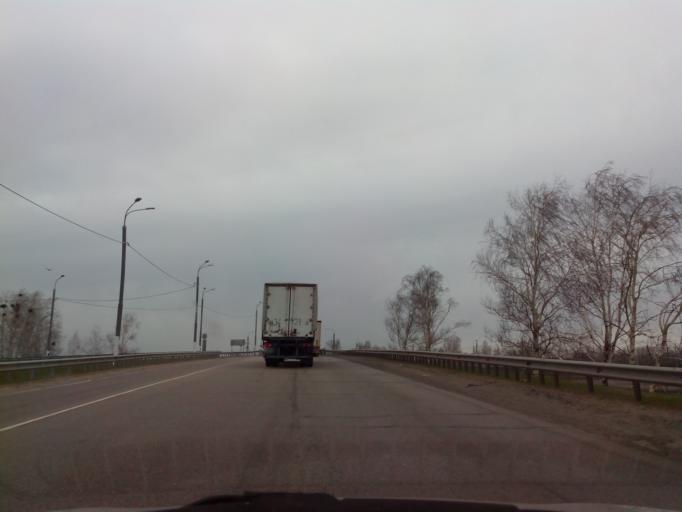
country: RU
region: Tambov
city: Komsomolets
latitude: 52.7320
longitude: 41.2964
